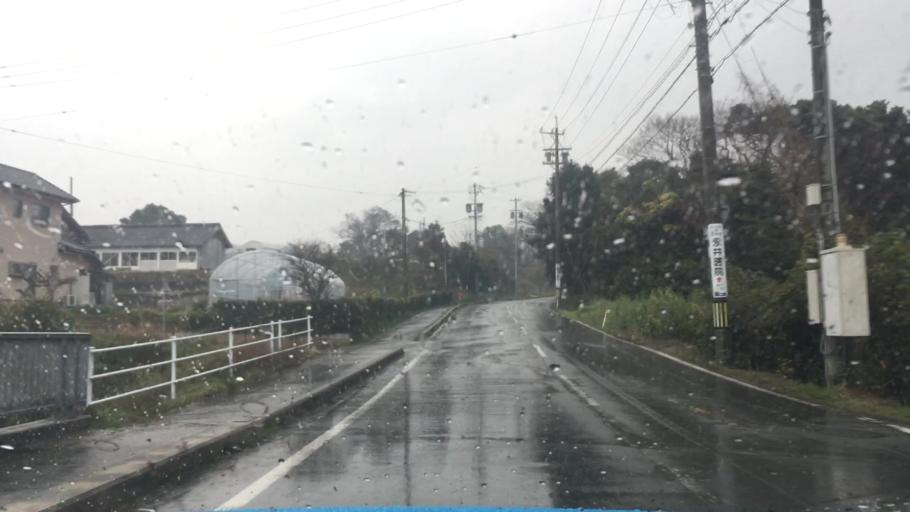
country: JP
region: Aichi
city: Tahara
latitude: 34.6455
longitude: 137.3065
